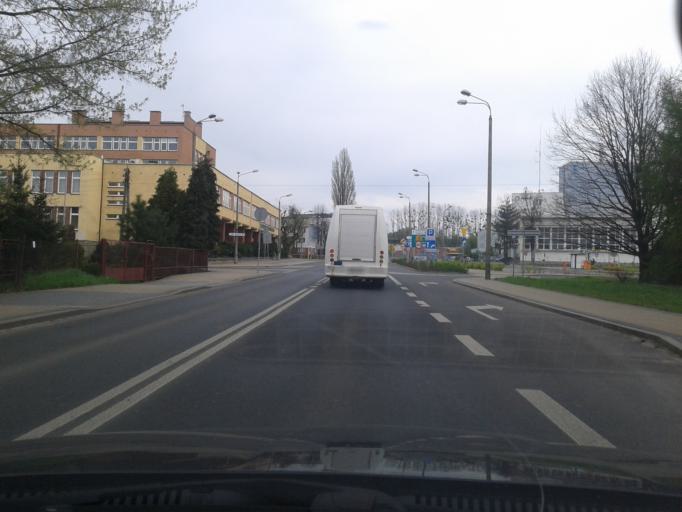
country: PL
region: Silesian Voivodeship
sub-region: Rybnik
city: Rybnik
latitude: 50.0891
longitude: 18.5395
